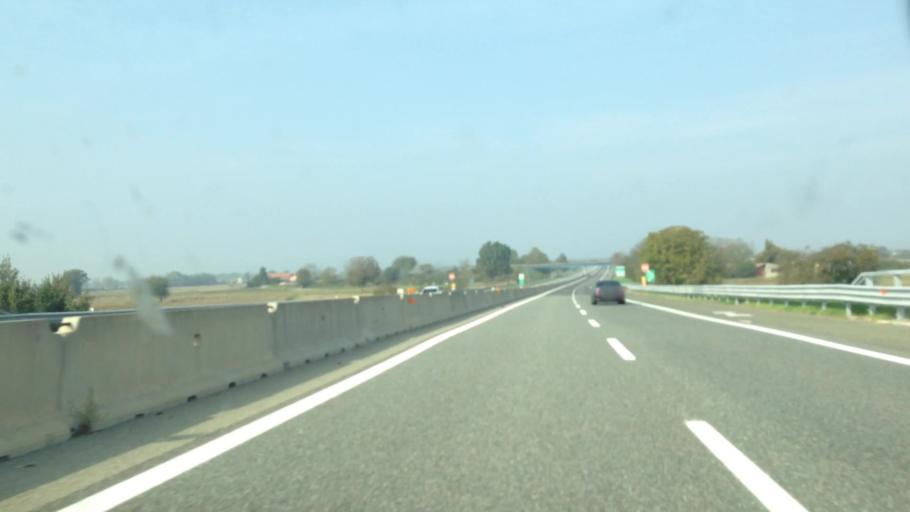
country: IT
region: Piedmont
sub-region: Provincia di Vercelli
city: Santhia
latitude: 45.3555
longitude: 8.1696
